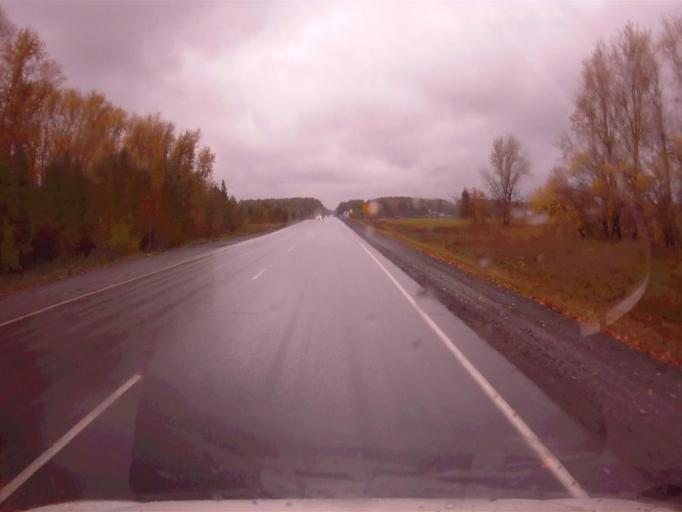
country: RU
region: Chelyabinsk
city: Argayash
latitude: 55.4541
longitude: 60.9311
